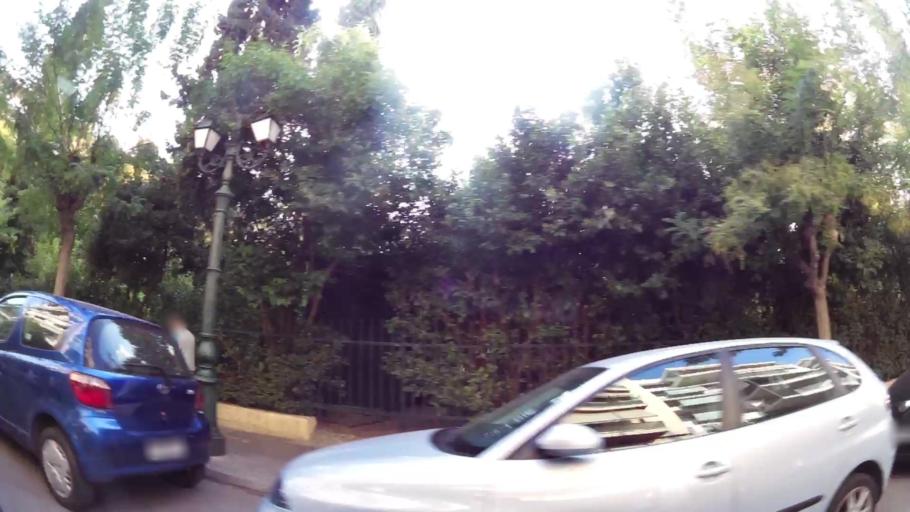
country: GR
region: Attica
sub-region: Nomarchia Athinas
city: Kallithea
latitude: 37.9558
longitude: 23.7039
